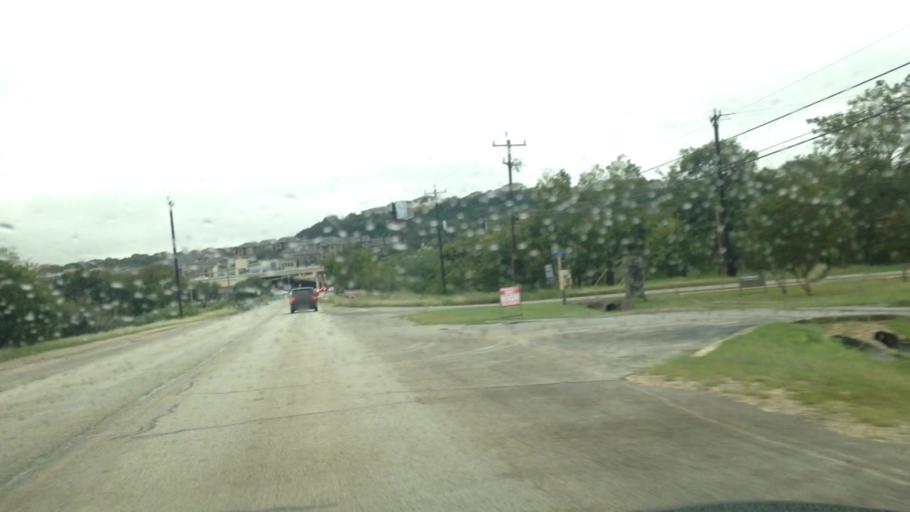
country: US
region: Texas
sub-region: Bexar County
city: Cross Mountain
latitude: 29.6275
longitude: -98.6069
